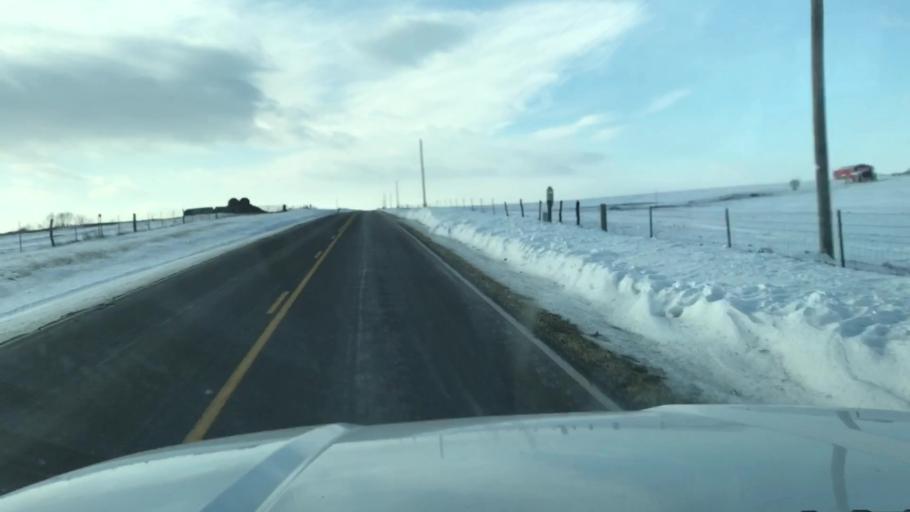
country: US
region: Missouri
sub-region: Nodaway County
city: Maryville
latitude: 40.2010
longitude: -94.9014
